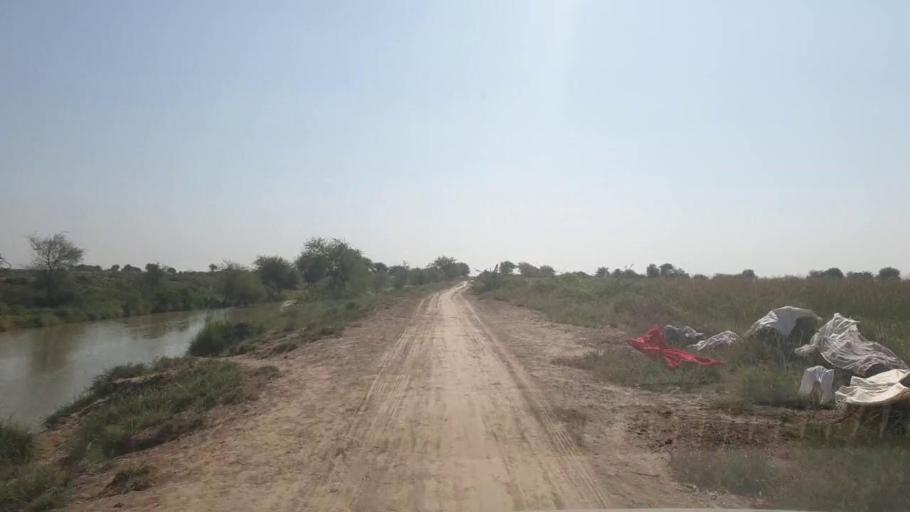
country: PK
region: Sindh
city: Tando Bago
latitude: 24.8897
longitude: 69.1645
